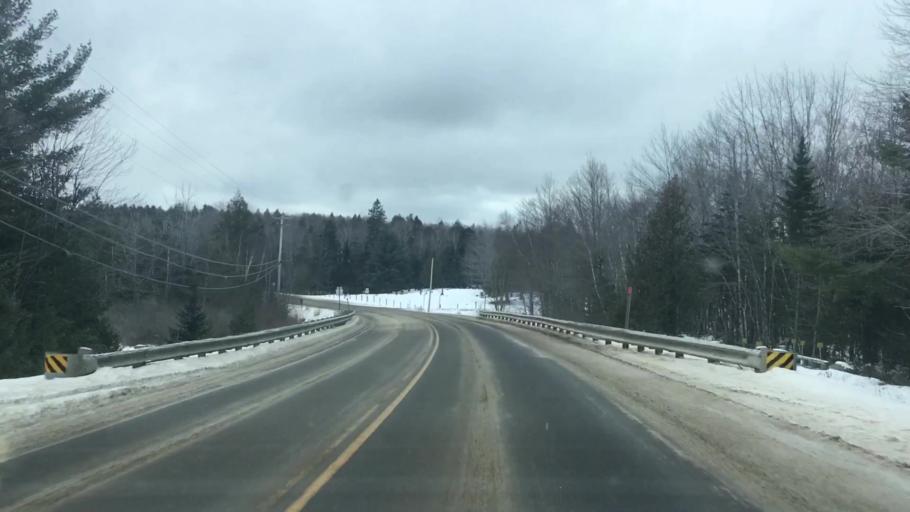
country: US
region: Maine
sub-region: Washington County
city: Calais
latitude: 45.0057
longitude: -67.4156
